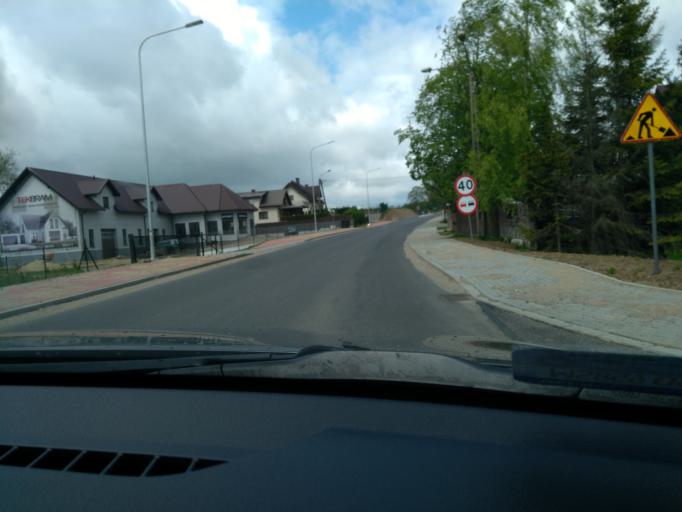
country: PL
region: Pomeranian Voivodeship
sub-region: Powiat kartuski
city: Chmielno
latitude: 54.3420
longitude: 18.0547
